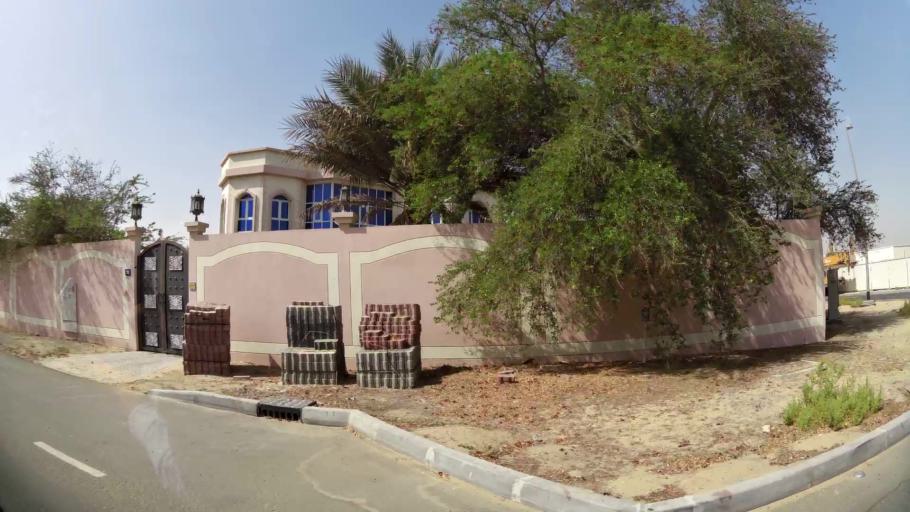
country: AE
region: Ash Shariqah
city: Sharjah
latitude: 25.2029
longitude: 55.4134
